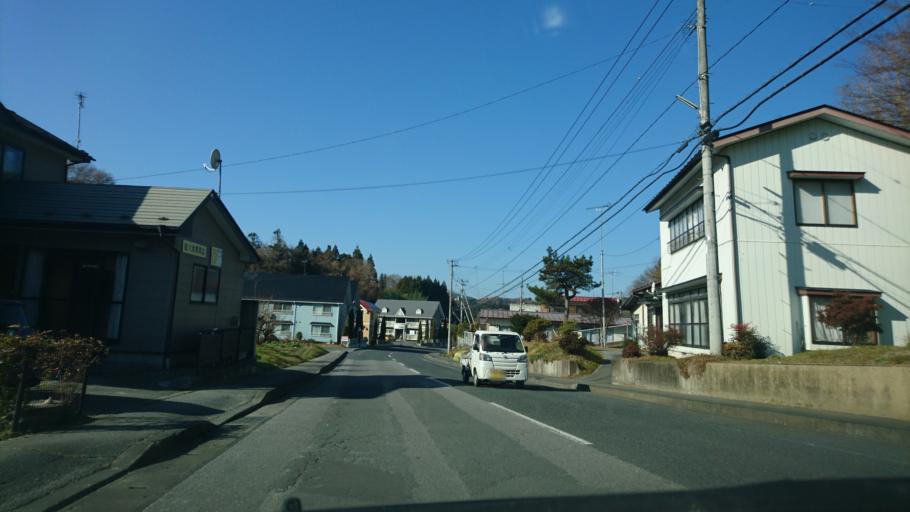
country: JP
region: Iwate
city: Ichinoseki
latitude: 38.9156
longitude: 141.3430
